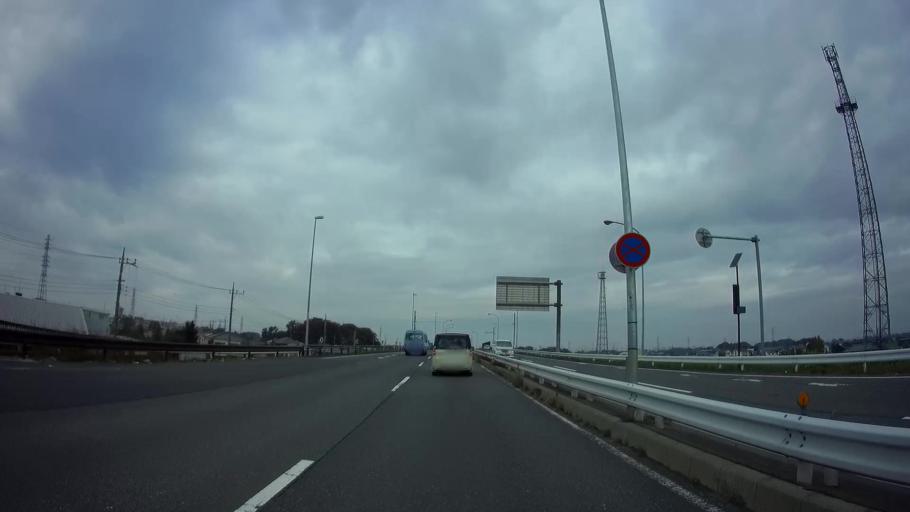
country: JP
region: Saitama
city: Kumagaya
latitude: 36.1687
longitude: 139.3786
